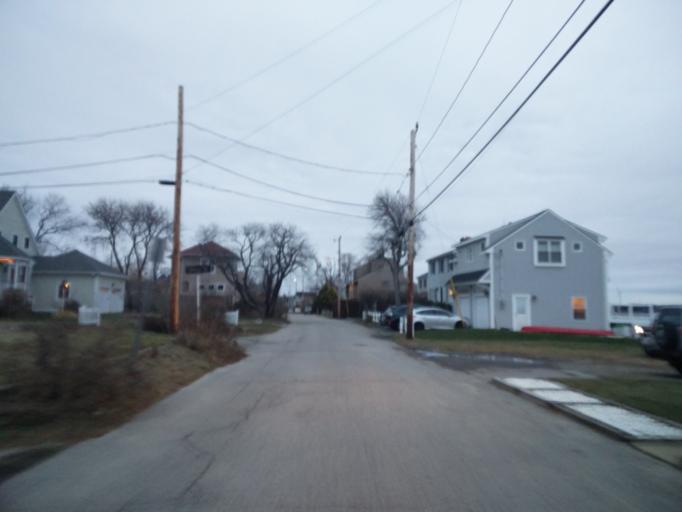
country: US
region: Massachusetts
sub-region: Plymouth County
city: Hingham
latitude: 42.2768
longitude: -70.8801
